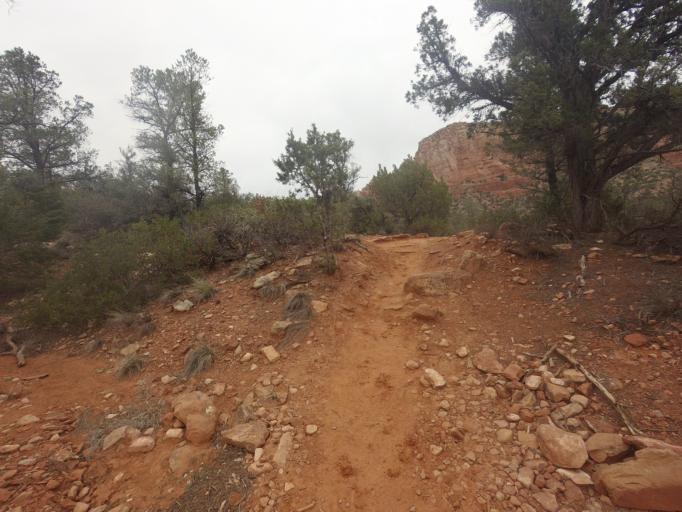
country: US
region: Arizona
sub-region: Yavapai County
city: Village of Oak Creek (Big Park)
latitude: 34.8024
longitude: -111.7472
